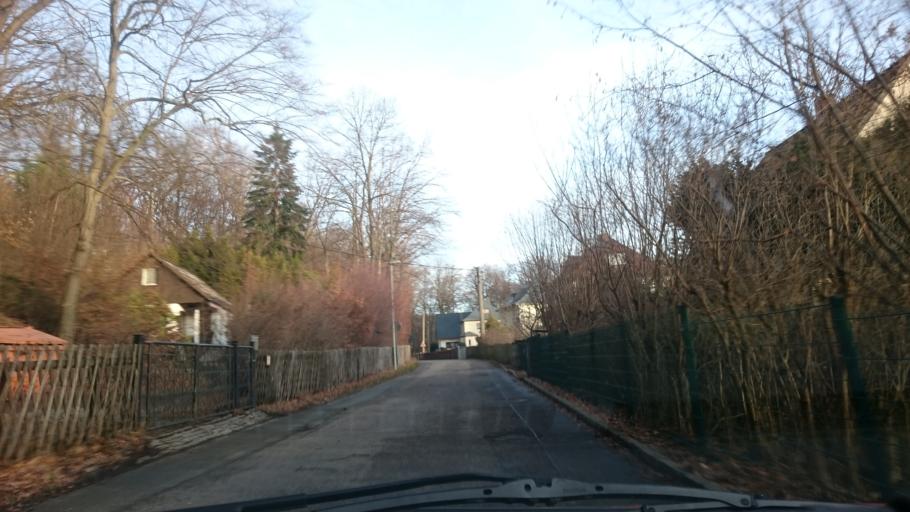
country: DE
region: Saxony
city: Zwickau
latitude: 50.7409
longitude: 12.5079
